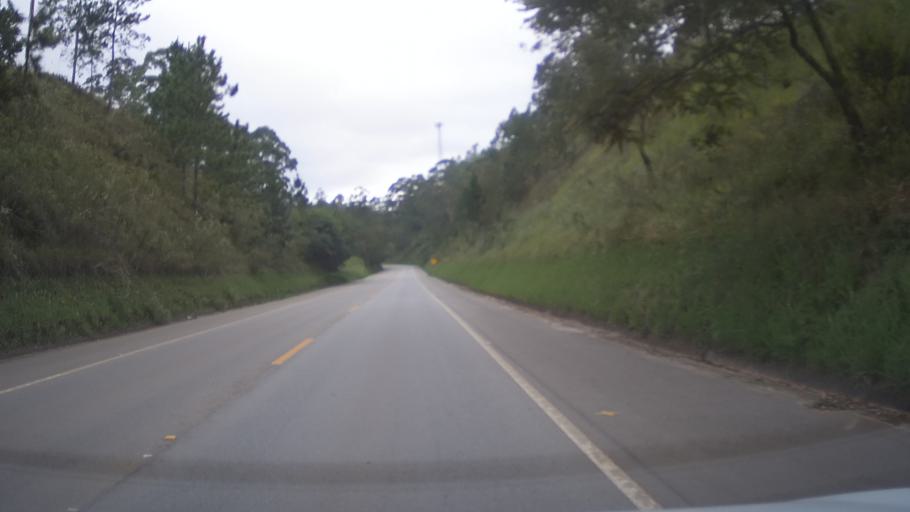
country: BR
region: Sao Paulo
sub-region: Aruja
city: Aruja
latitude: -23.3578
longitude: -46.4169
